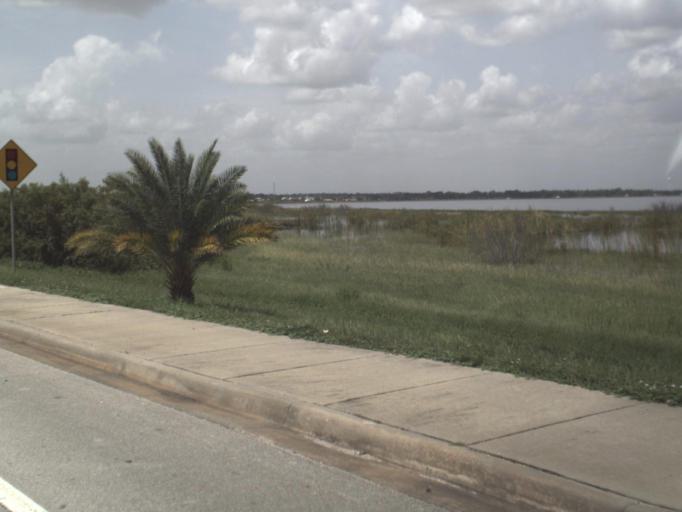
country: US
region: Florida
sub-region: Highlands County
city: Sebring
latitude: 27.4716
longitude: -81.4633
